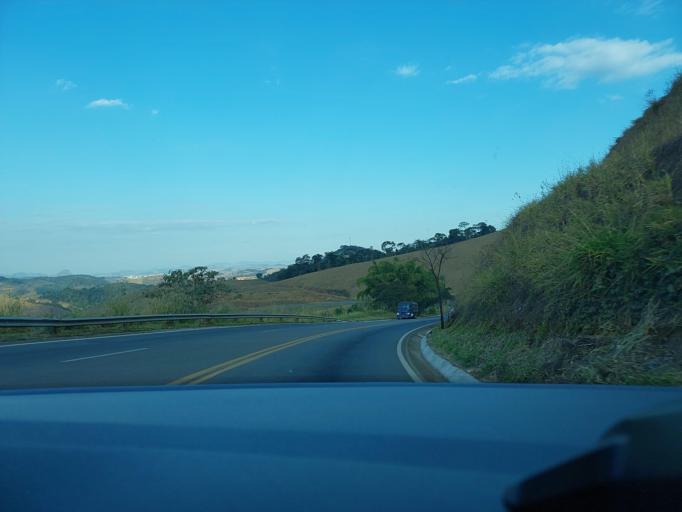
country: BR
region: Minas Gerais
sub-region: Muriae
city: Muriae
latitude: -21.0894
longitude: -42.4829
